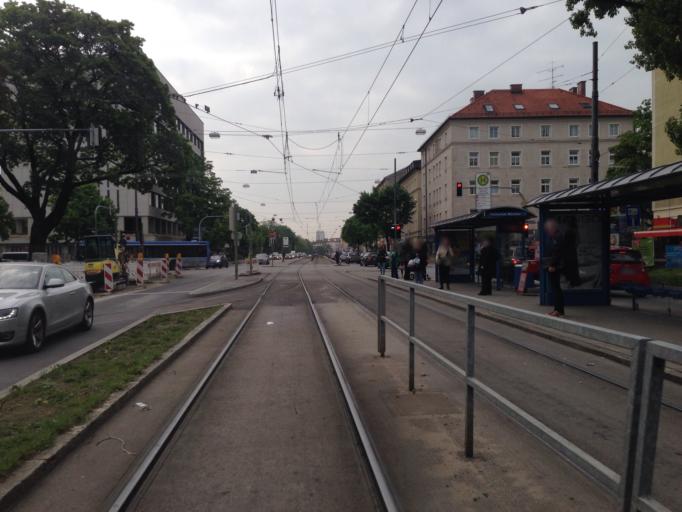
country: DE
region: Bavaria
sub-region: Upper Bavaria
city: Munich
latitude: 48.1546
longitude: 11.5534
